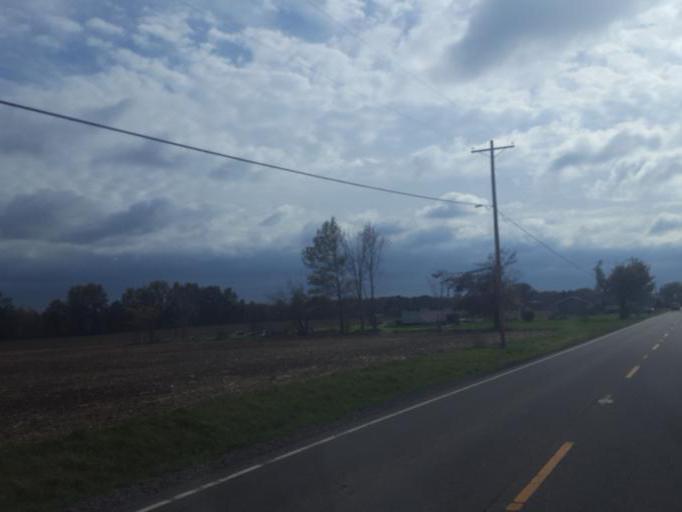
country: US
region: Ohio
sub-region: Crawford County
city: Crestline
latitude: 40.8040
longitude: -82.7877
